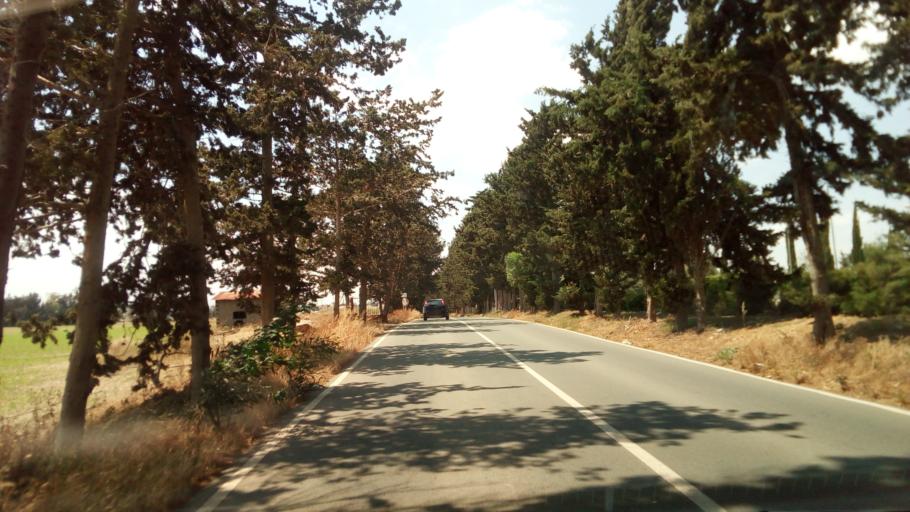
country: CY
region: Larnaka
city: Meneou
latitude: 34.8544
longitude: 33.6038
